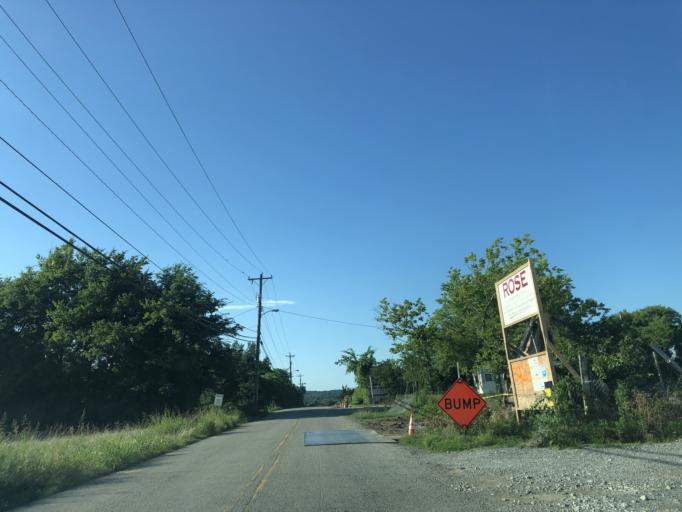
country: US
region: Tennessee
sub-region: Davidson County
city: Nashville
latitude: 36.1975
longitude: -86.8620
